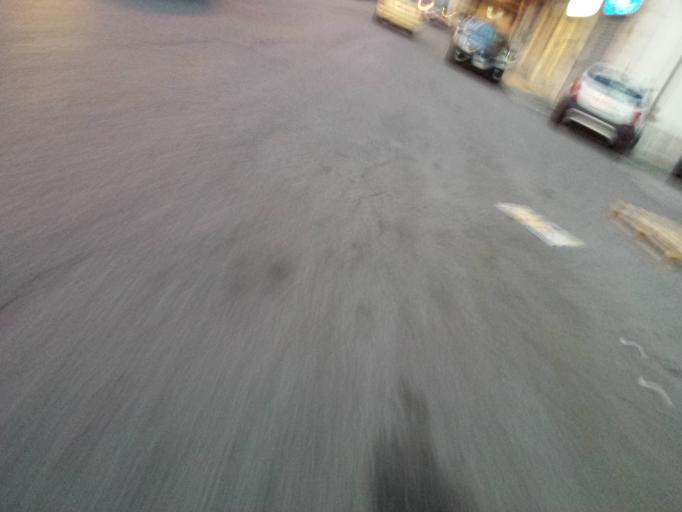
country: IT
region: Molise
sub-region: Provincia di Campobasso
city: Campobasso
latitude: 41.5653
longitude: 14.6724
